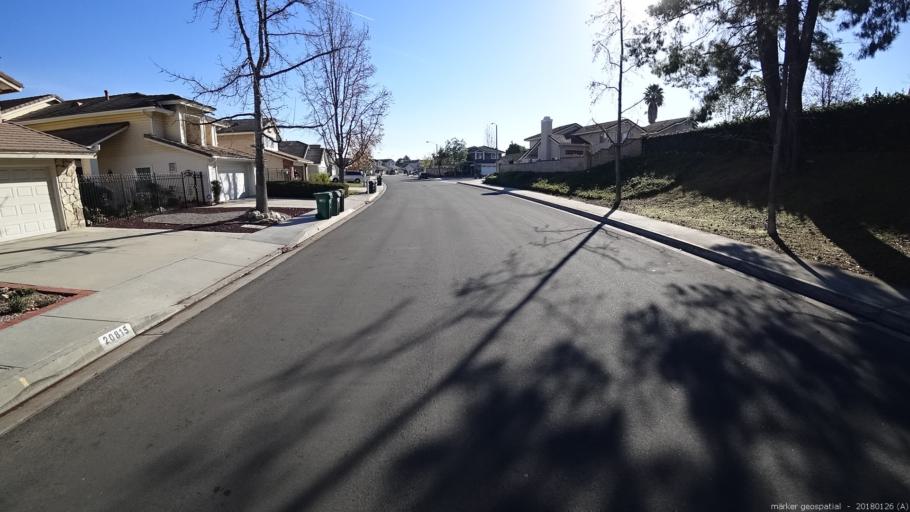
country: US
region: California
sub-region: Los Angeles County
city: Walnut
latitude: 33.9769
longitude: -117.8521
